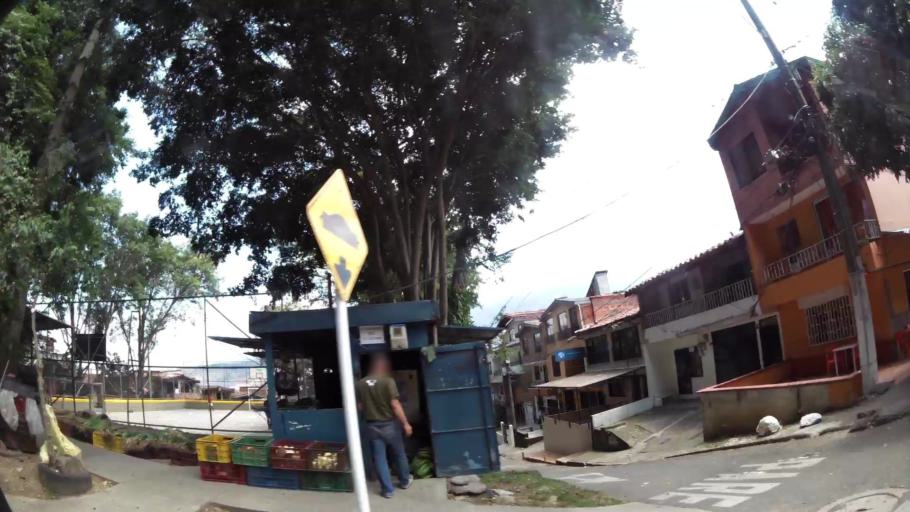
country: CO
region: Antioquia
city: Bello
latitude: 6.3054
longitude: -75.5688
